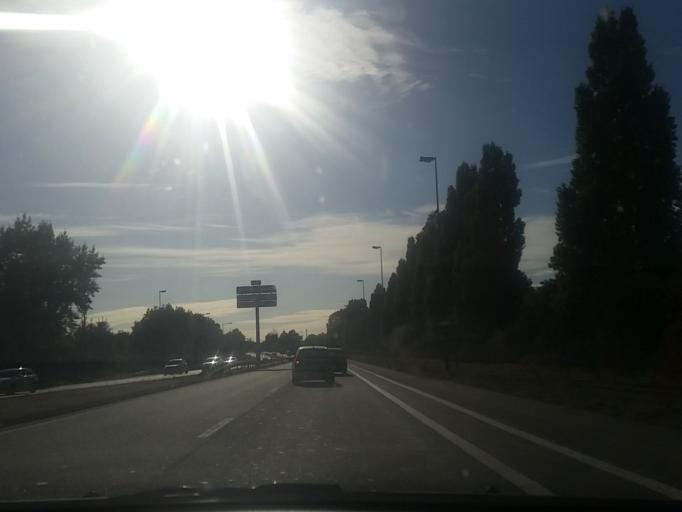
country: FR
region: Pays de la Loire
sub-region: Departement de la Loire-Atlantique
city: Reze
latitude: 47.1929
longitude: -1.5643
